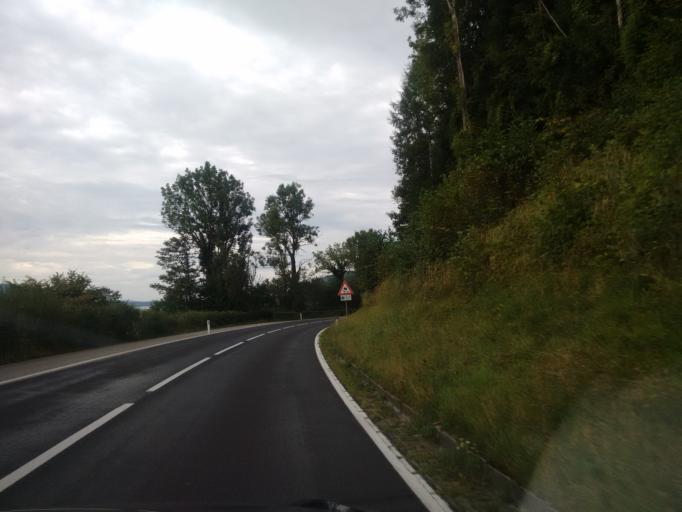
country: AT
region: Upper Austria
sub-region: Politischer Bezirk Vocklabruck
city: Steinbach am Attersee
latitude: 47.8588
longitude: 13.5591
